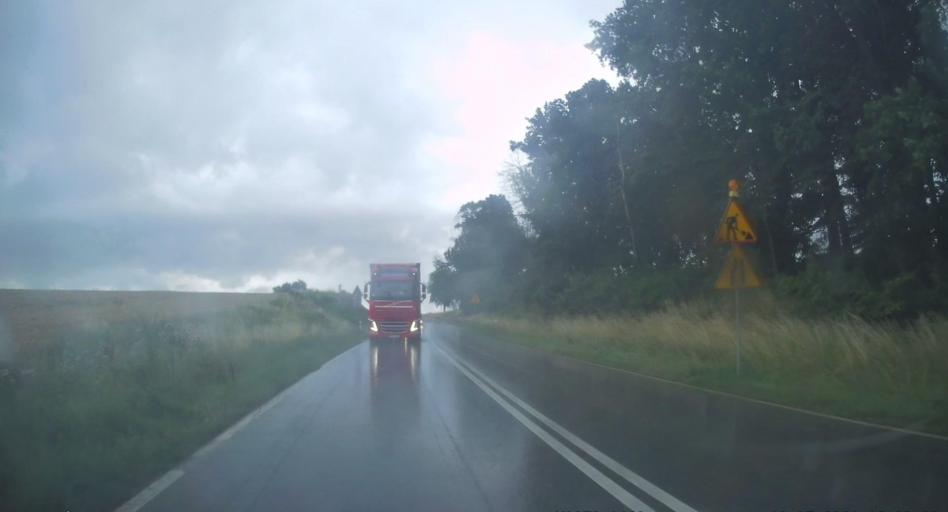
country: PL
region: Opole Voivodeship
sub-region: Powiat nyski
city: Nysa
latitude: 50.4319
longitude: 17.4203
